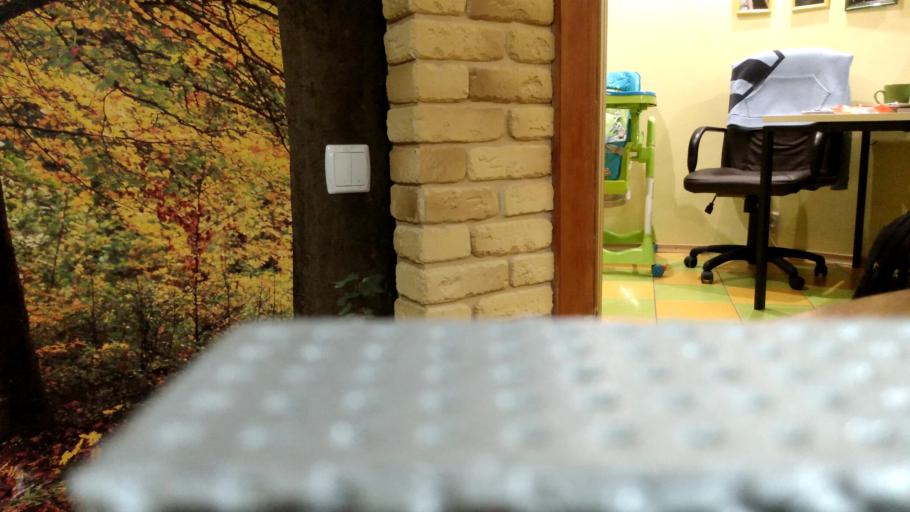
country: RU
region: Republic of Karelia
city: Pudozh
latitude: 61.9179
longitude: 37.6292
